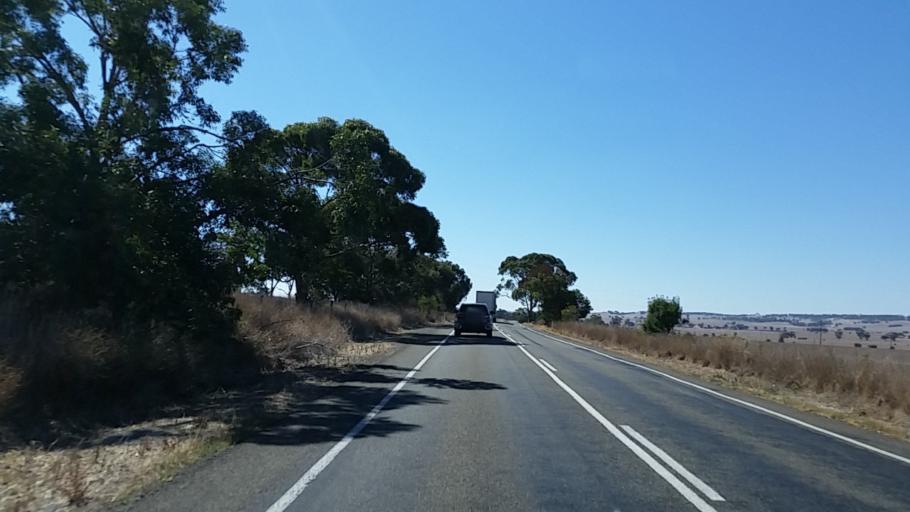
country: AU
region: South Australia
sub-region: Clare and Gilbert Valleys
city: Clare
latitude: -34.0236
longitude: 138.8056
